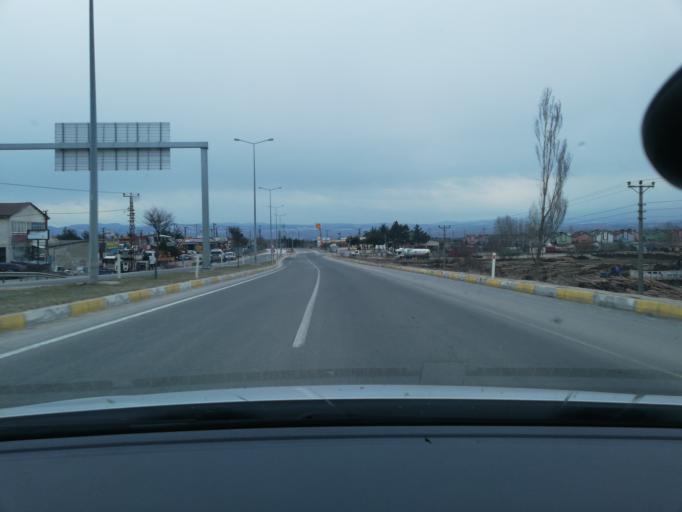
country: TR
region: Bolu
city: Gerede
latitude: 40.7896
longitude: 32.2084
